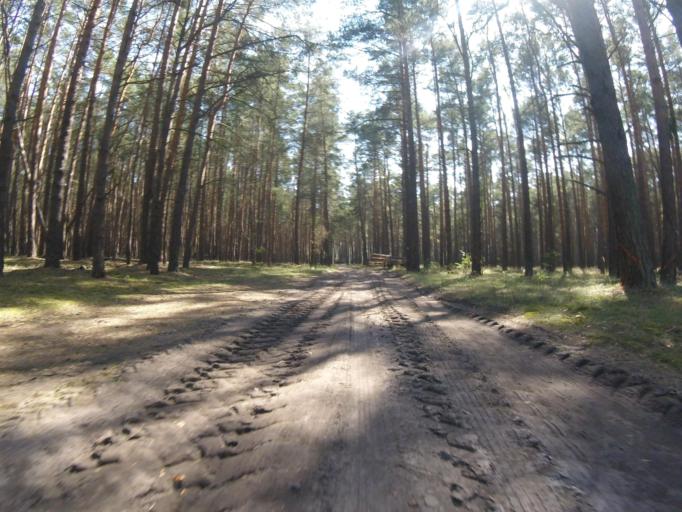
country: DE
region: Brandenburg
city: Bestensee
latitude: 52.2599
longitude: 13.6884
